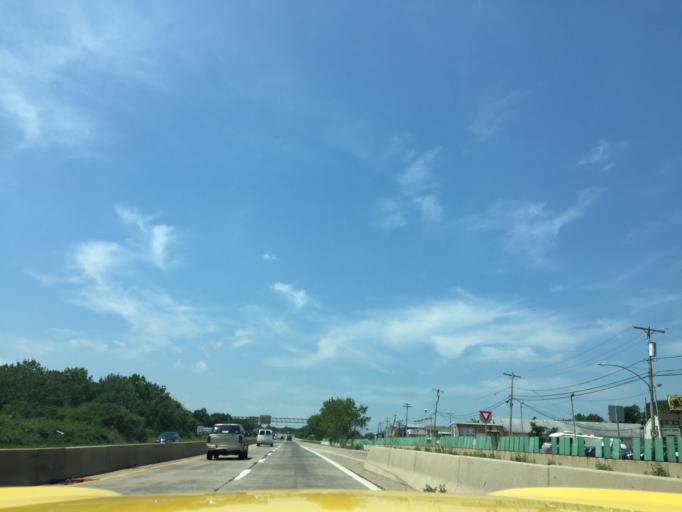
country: US
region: Pennsylvania
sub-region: Bucks County
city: Morrisville
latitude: 40.1966
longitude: -74.8051
